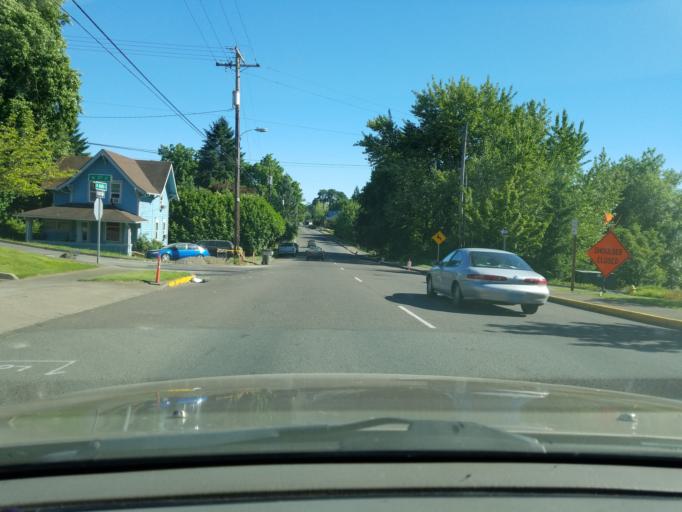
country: US
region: Oregon
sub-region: Yamhill County
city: McMinnville
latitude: 45.2088
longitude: -123.1991
